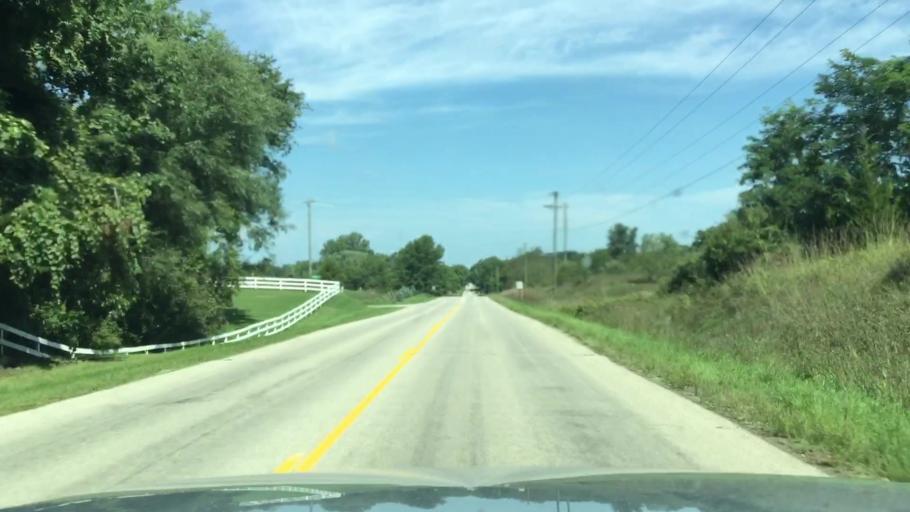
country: US
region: Michigan
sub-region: Lenawee County
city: Manitou Beach-Devils Lake
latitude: 42.0331
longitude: -84.2763
